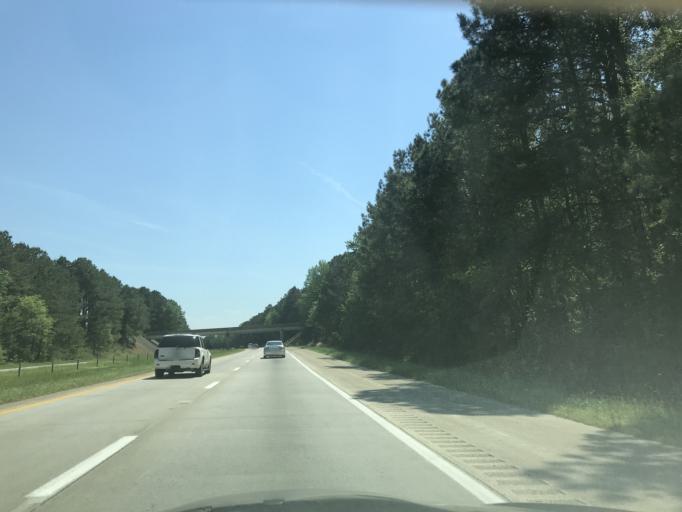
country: US
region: North Carolina
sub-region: Johnston County
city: Benson
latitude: 35.4740
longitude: -78.5497
